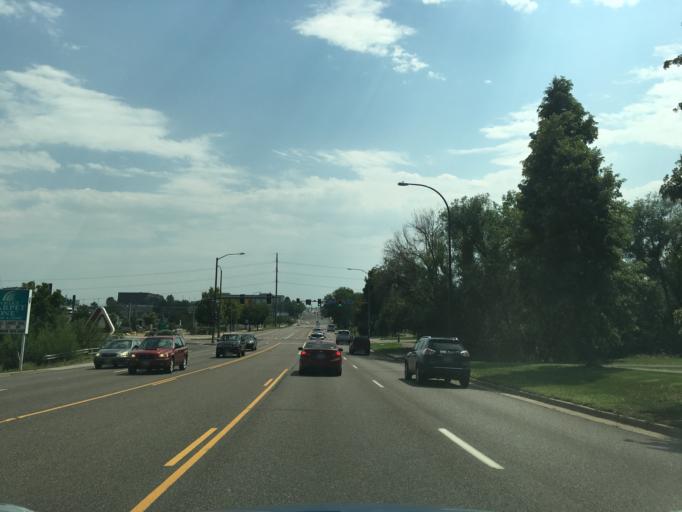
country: US
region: Colorado
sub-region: Jefferson County
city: Applewood
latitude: 39.7355
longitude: -105.1285
